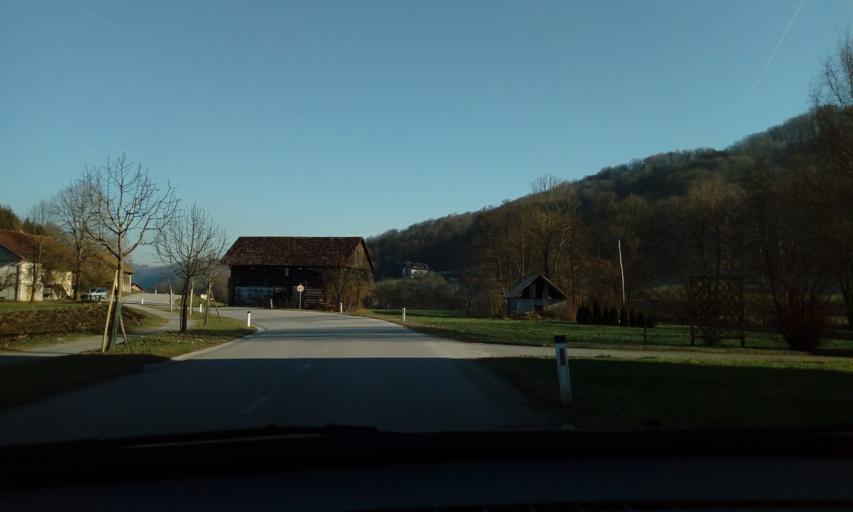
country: SI
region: Podcetrtek
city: Podcetrtek
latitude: 46.1453
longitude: 15.5792
